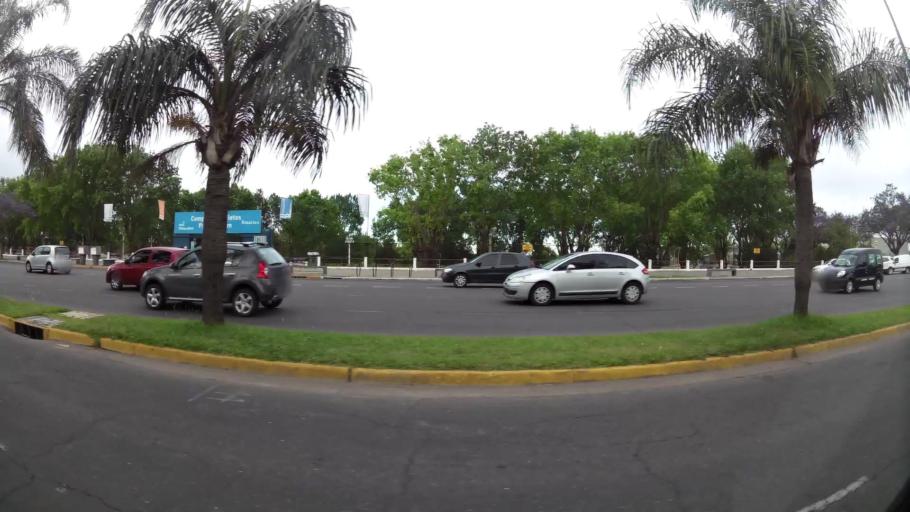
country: AR
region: Santa Fe
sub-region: Departamento de Rosario
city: Rosario
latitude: -32.9107
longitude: -60.6772
